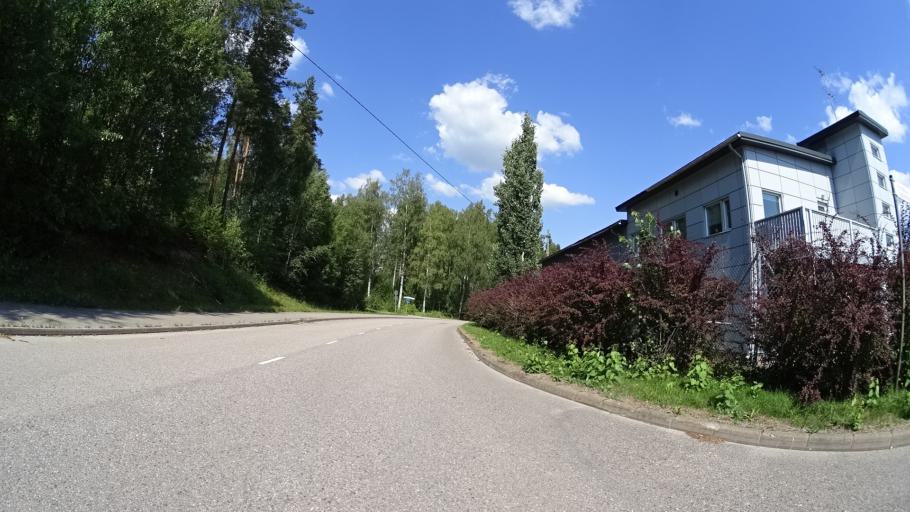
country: FI
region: Uusimaa
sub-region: Helsinki
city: Teekkarikylae
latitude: 60.3014
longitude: 24.8805
